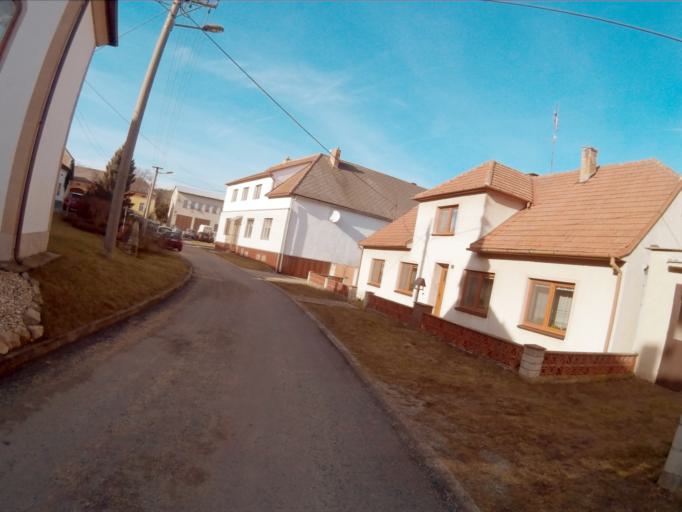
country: CZ
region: Vysocina
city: Mohelno
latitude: 49.1453
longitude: 16.1711
